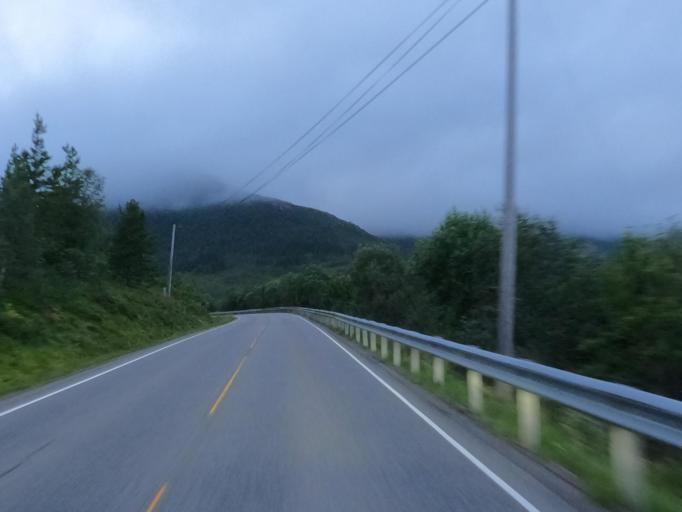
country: NO
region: Nordland
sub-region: Lodingen
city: Lodingen
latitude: 68.6124
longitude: 15.7742
